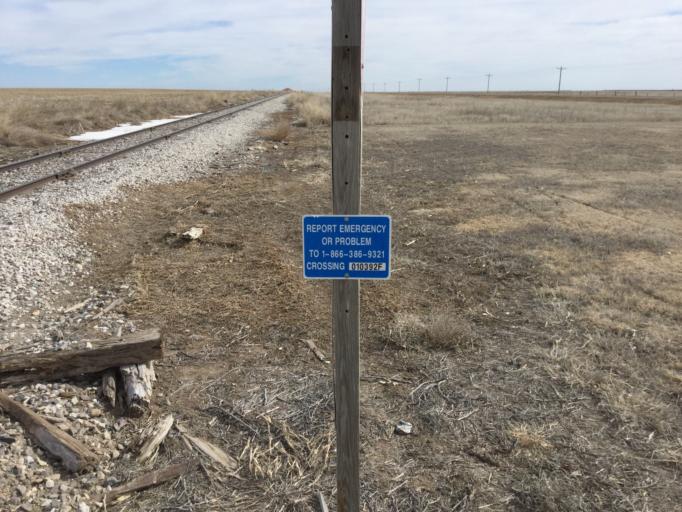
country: US
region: Kansas
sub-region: Lane County
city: Dighton
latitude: 38.4824
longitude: -100.5587
